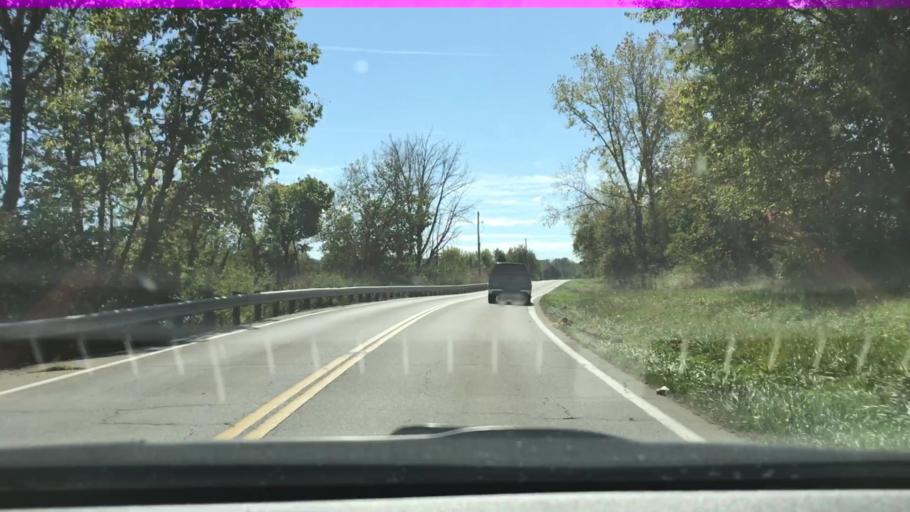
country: US
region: Ohio
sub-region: Butler County
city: Hamilton
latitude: 39.4640
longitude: -84.6288
